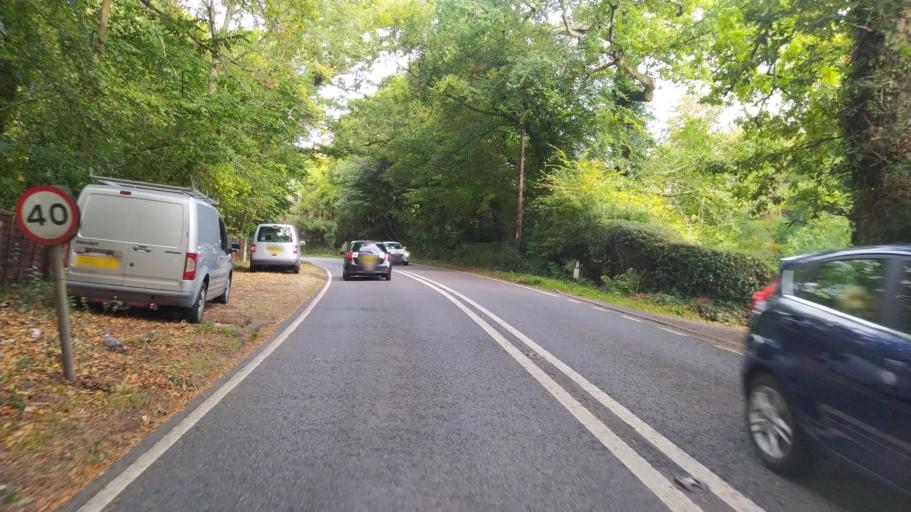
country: GB
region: England
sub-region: Hampshire
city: Lymington
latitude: 50.7741
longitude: -1.5521
